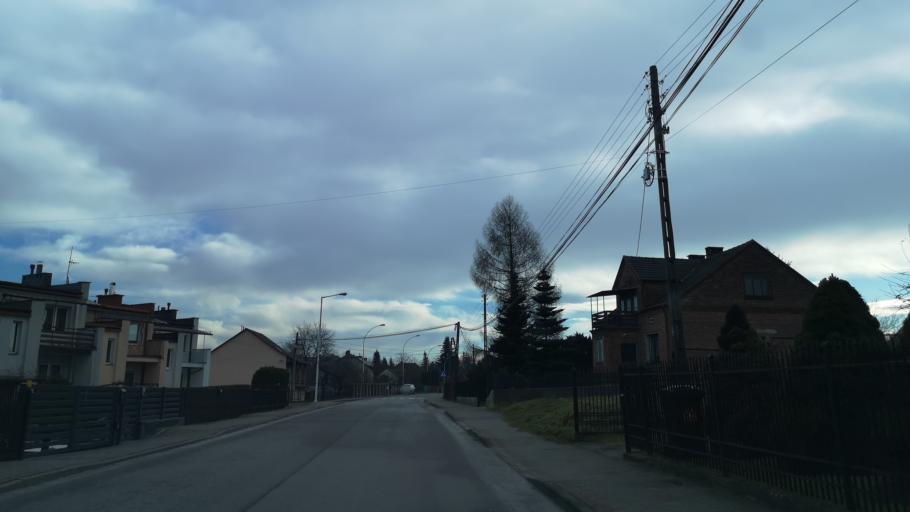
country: PL
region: Subcarpathian Voivodeship
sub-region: Powiat lezajski
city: Lezajsk
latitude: 50.2590
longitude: 22.4130
